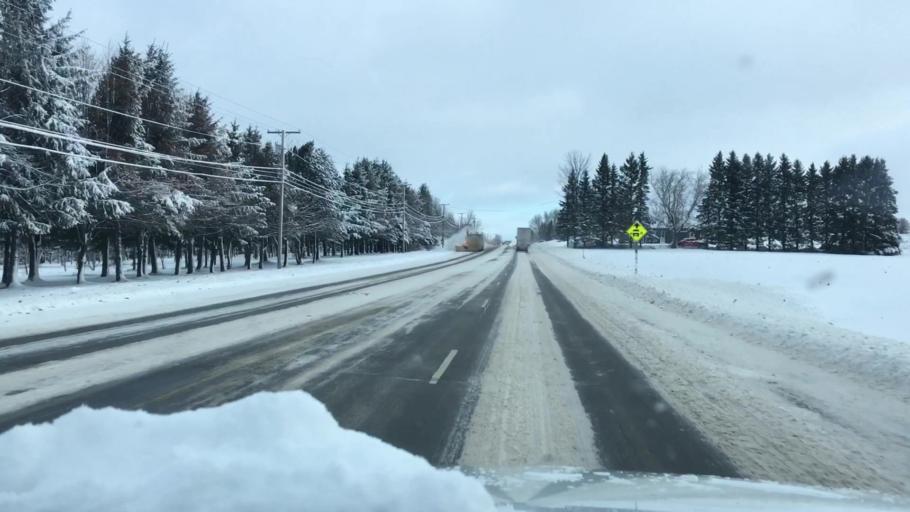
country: US
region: Maine
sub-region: Aroostook County
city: Presque Isle
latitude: 46.7225
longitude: -68.0057
